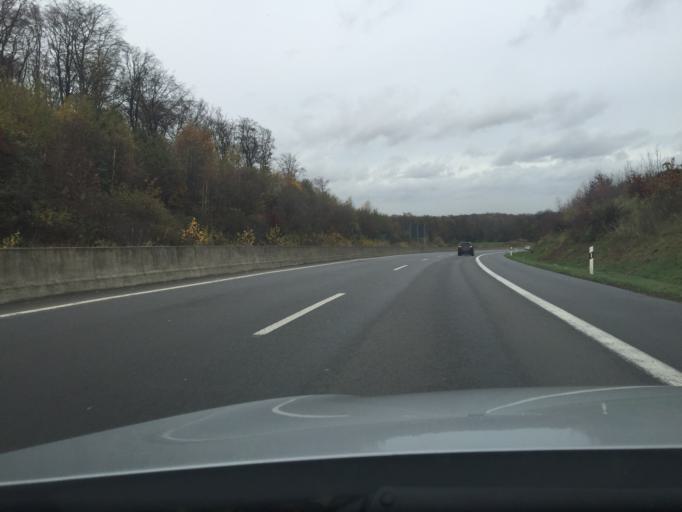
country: DE
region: North Rhine-Westphalia
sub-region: Regierungsbezirk Dusseldorf
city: Velbert
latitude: 51.3690
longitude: 7.0714
